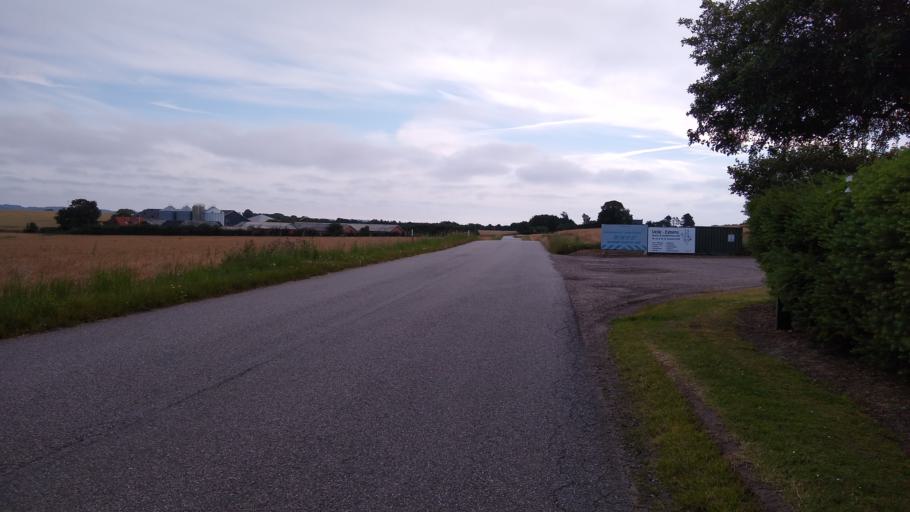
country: DK
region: South Denmark
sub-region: Vejle Kommune
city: Brejning
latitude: 55.6484
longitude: 9.7231
